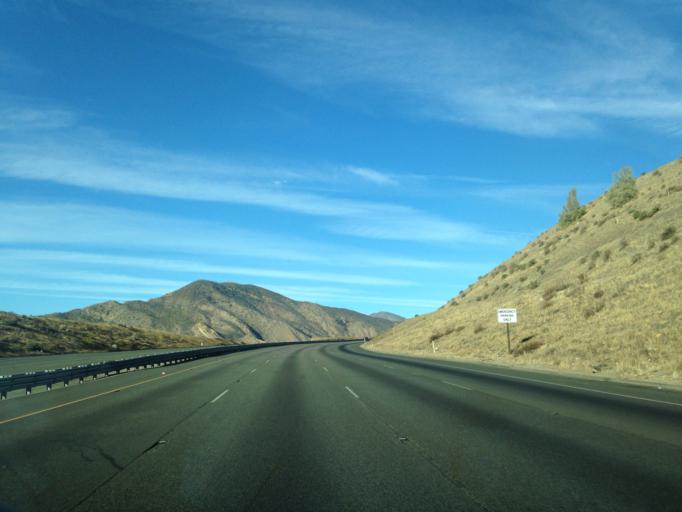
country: US
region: California
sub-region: Los Angeles County
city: Castaic
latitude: 34.6349
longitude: -118.7359
